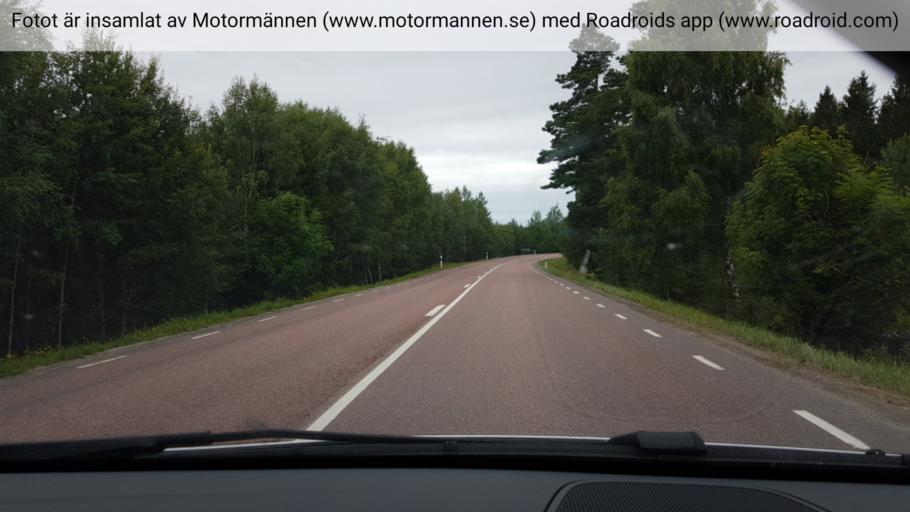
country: SE
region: Soedermanland
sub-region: Strangnas Kommun
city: Mariefred
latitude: 59.2174
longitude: 17.3068
